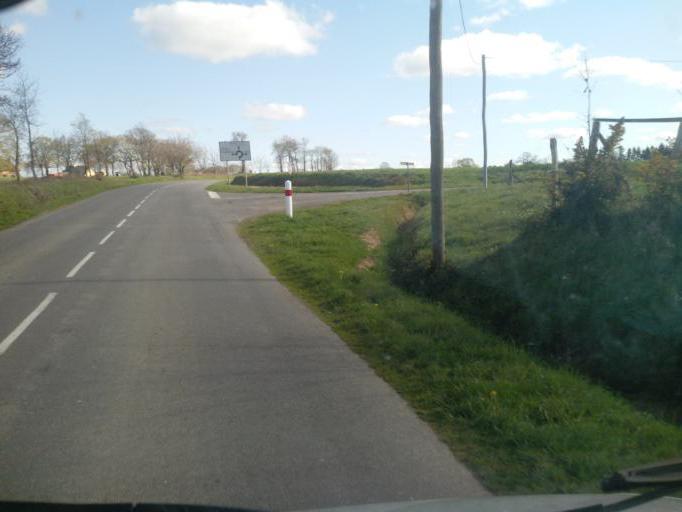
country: FR
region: Brittany
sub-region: Departement d'Ille-et-Vilaine
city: Maure-de-Bretagne
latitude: 47.9141
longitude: -1.9924
